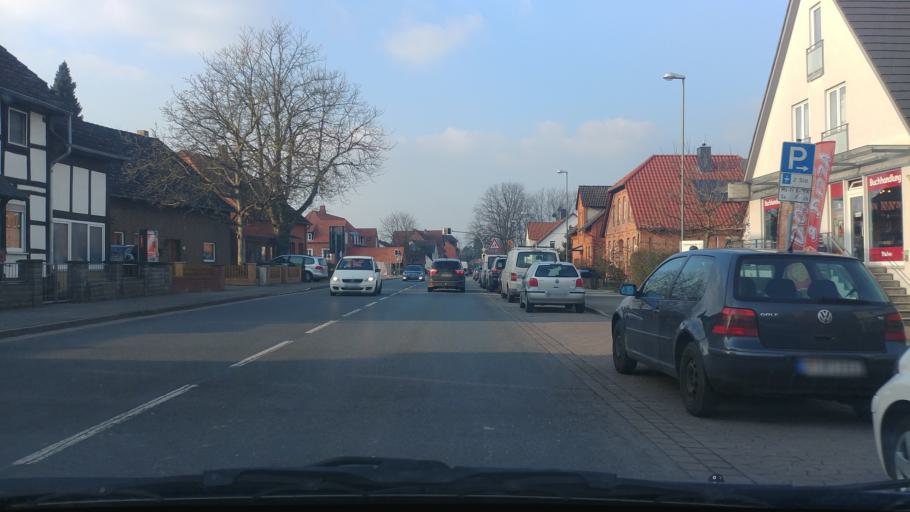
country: DE
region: Lower Saxony
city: Hemmingen
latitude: 52.3032
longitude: 9.7390
